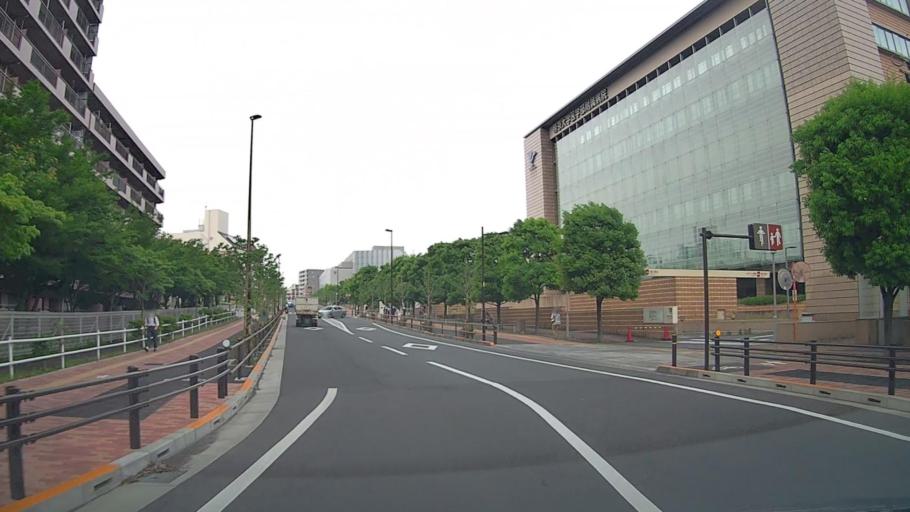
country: JP
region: Saitama
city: Kawaguchi
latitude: 35.7590
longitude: 139.7124
